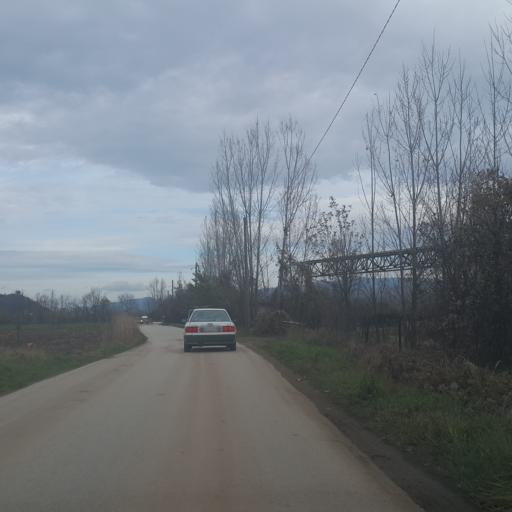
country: RS
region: Central Serbia
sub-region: Zajecarski Okrug
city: Knjazevac
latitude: 43.5830
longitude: 22.2488
